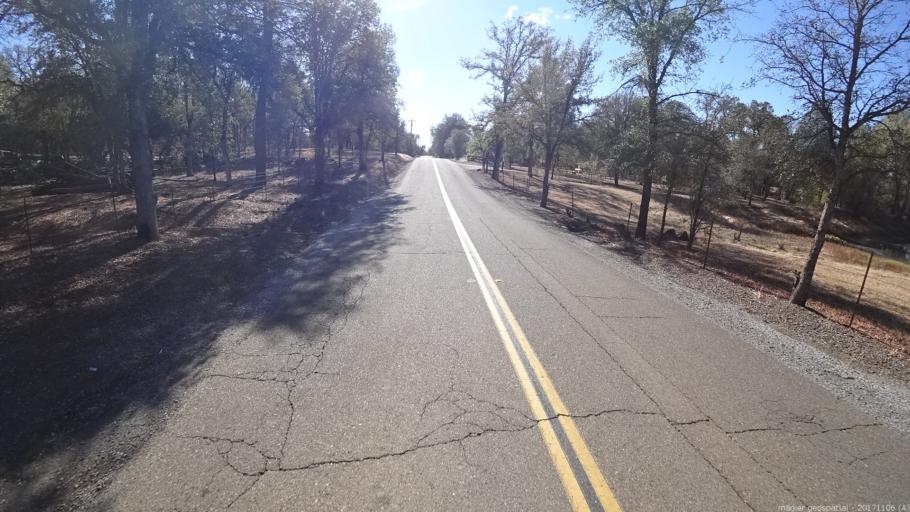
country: US
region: California
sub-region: Shasta County
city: Bella Vista
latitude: 40.6150
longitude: -122.2777
